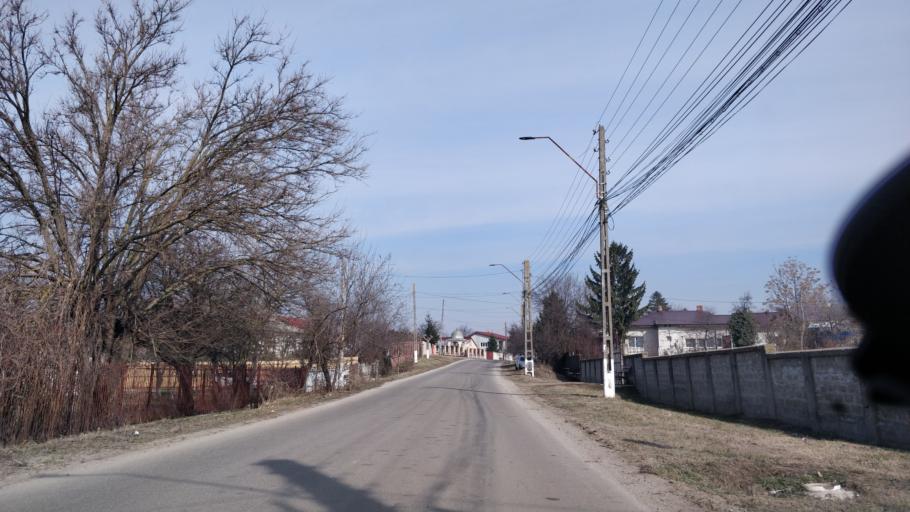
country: RO
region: Giurgiu
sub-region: Comuna Ulmi
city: Ulmi
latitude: 44.4850
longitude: 25.7774
